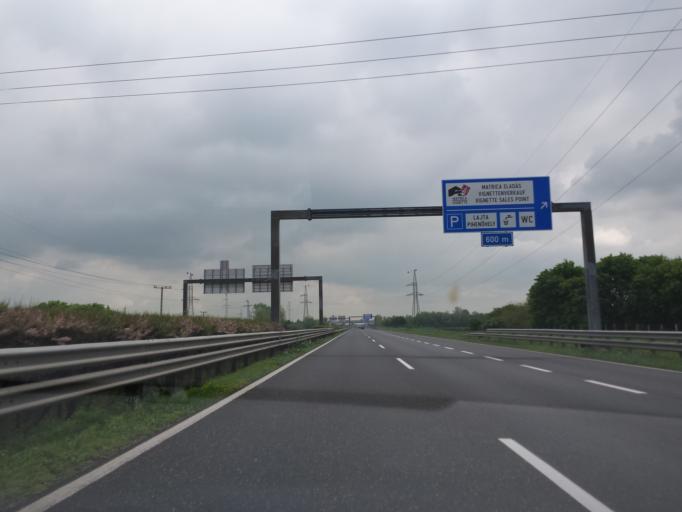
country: HU
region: Gyor-Moson-Sopron
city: Mosonmagyarovar
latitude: 47.8513
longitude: 17.2490
